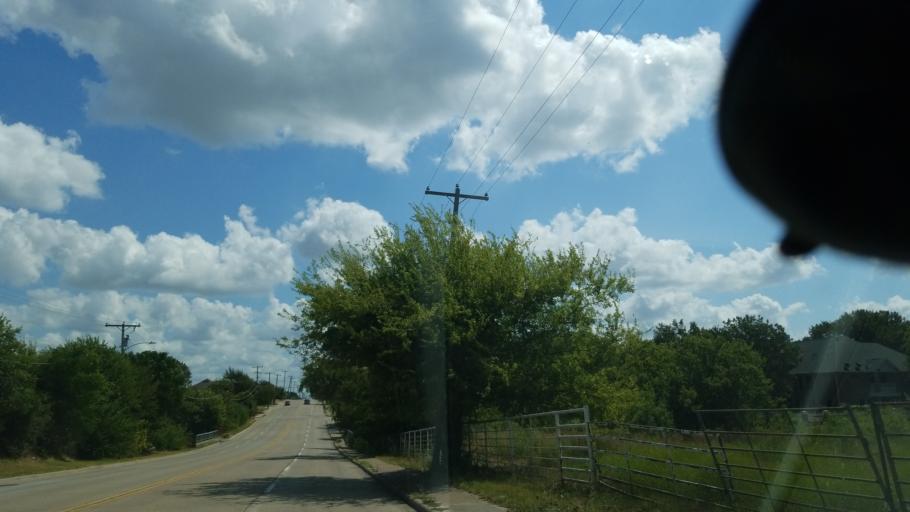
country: US
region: Texas
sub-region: Dallas County
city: Grand Prairie
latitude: 32.7205
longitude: -96.9931
